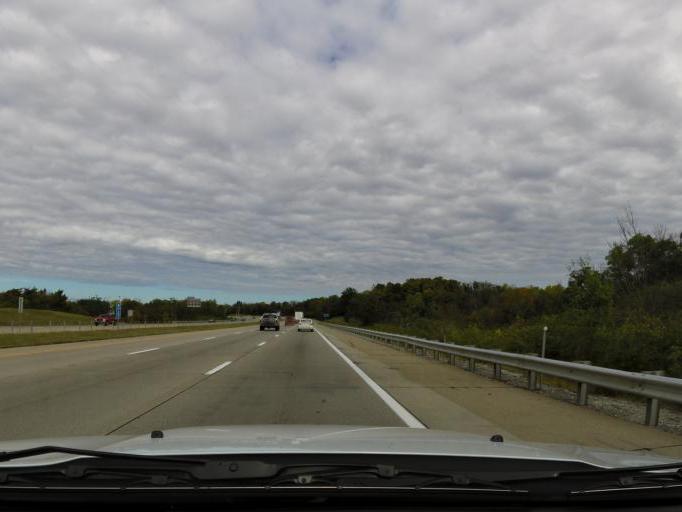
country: US
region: Ohio
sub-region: Hamilton County
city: Delhi Hills
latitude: 39.0646
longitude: -84.6449
